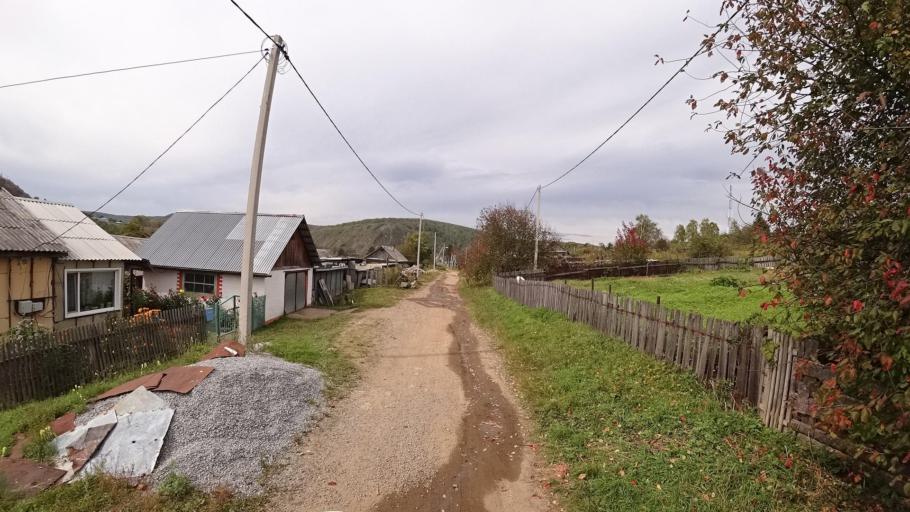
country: RU
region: Jewish Autonomous Oblast
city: Khingansk
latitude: 49.1231
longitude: 131.2071
